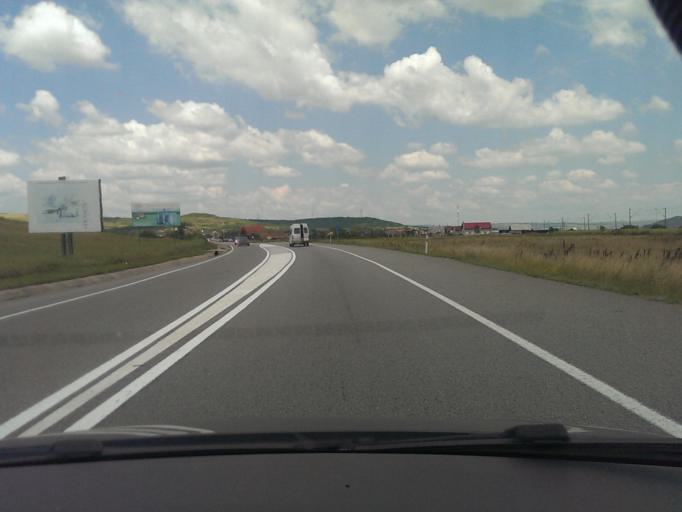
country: RO
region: Cluj
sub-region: Comuna Bontida
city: Rascruci
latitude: 46.8924
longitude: 23.7790
